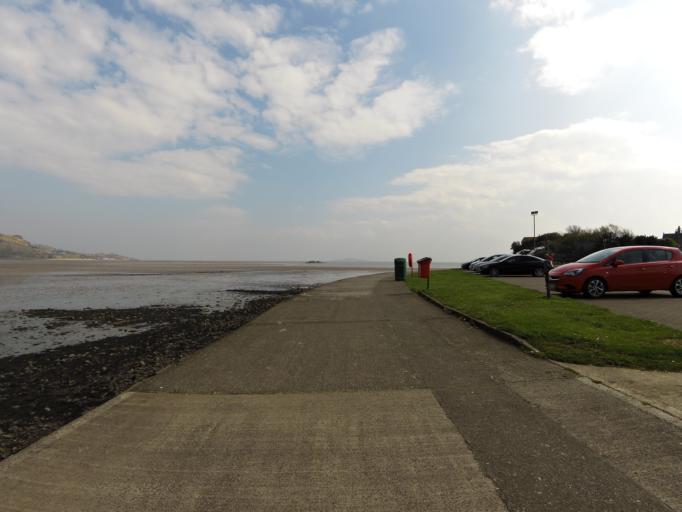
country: GB
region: Scotland
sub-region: Fife
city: Burntisland
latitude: 56.0600
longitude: -3.2248
